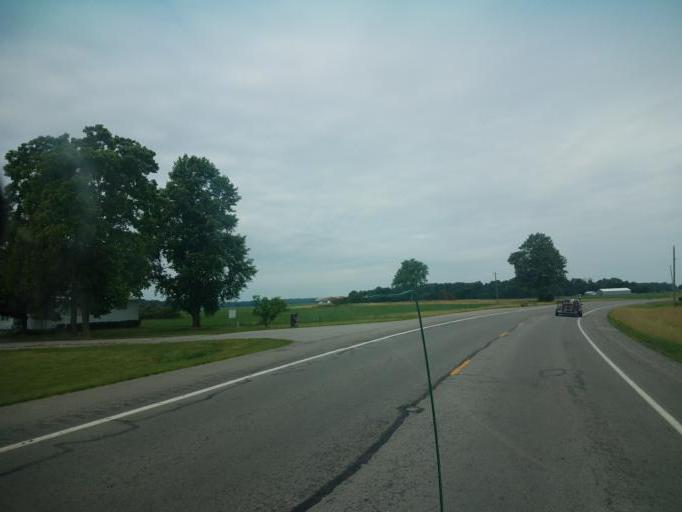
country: US
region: Ohio
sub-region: Hardin County
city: Ada
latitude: 40.7184
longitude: -83.7692
